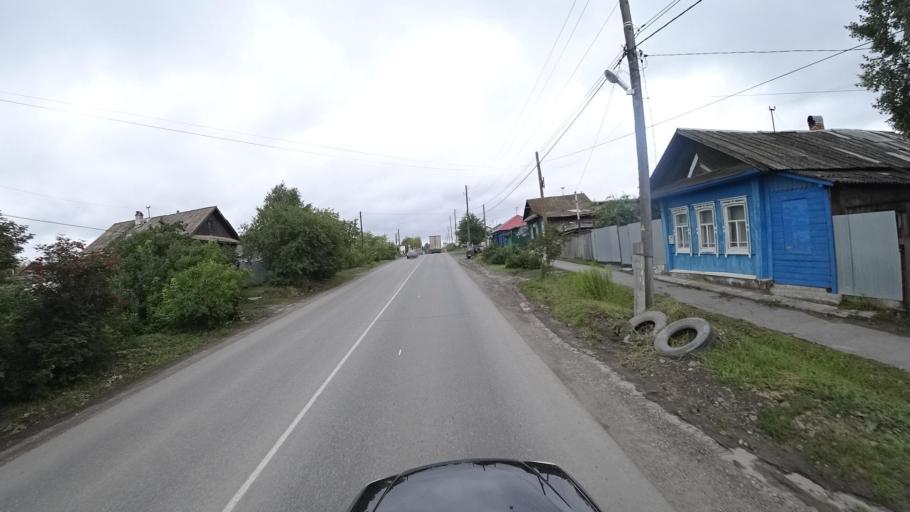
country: RU
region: Sverdlovsk
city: Kamyshlov
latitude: 56.8414
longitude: 62.7248
